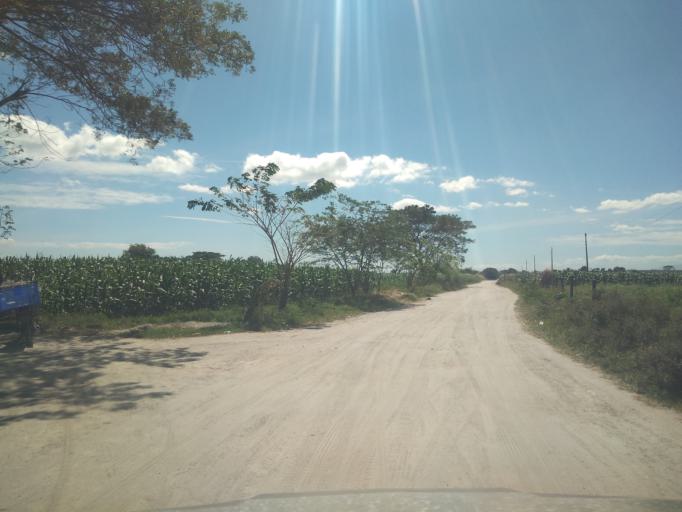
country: PH
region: Central Luzon
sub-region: Province of Pampanga
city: San Basilio
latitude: 15.0281
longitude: 120.6053
